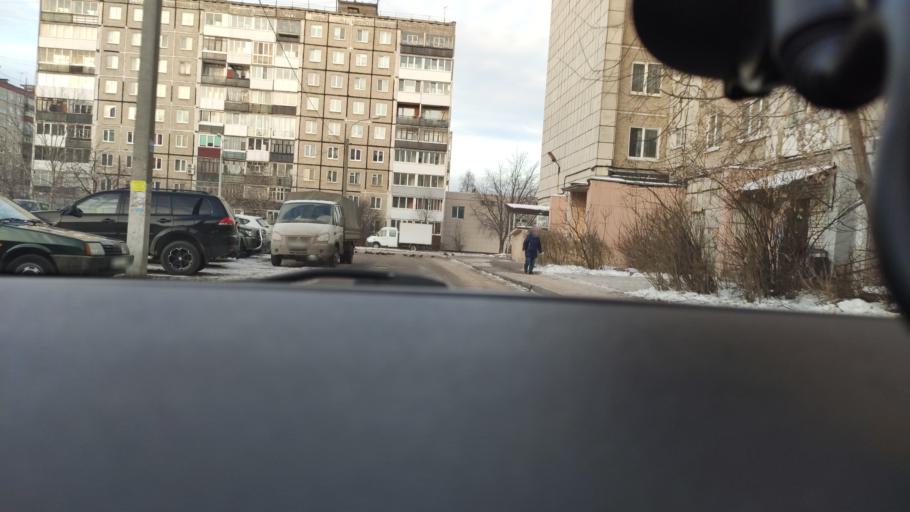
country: RU
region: Perm
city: Perm
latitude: 58.1103
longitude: 56.2889
